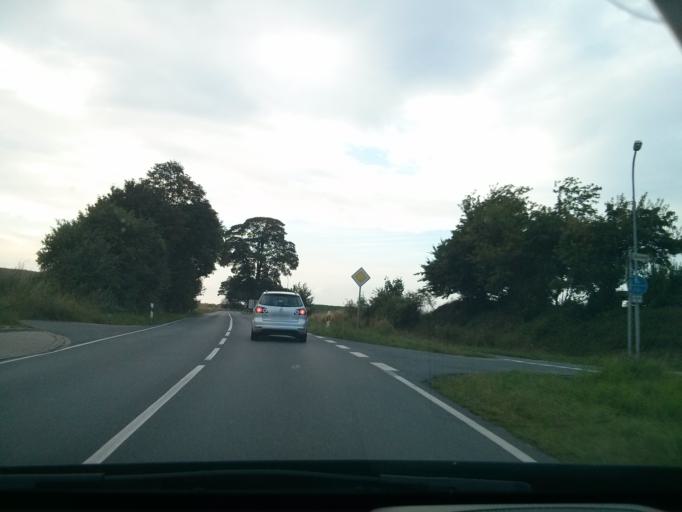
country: DE
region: Lower Saxony
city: Harmstorf
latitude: 53.3743
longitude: 9.9838
